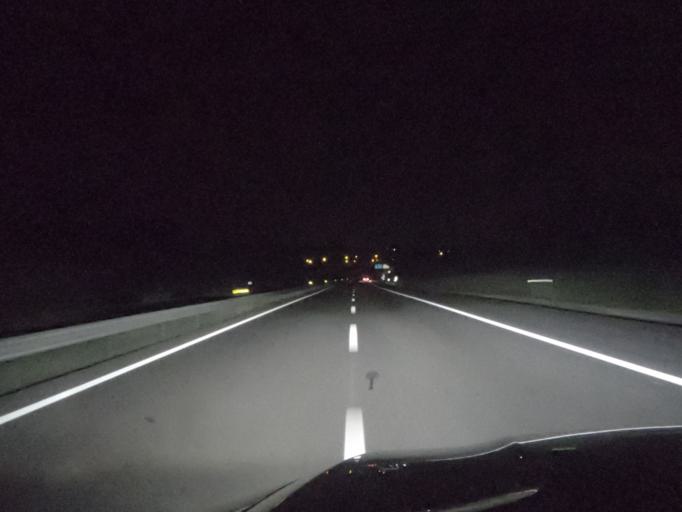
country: PT
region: Aveiro
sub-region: Mealhada
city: Mealhada
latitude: 40.3668
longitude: -8.4929
